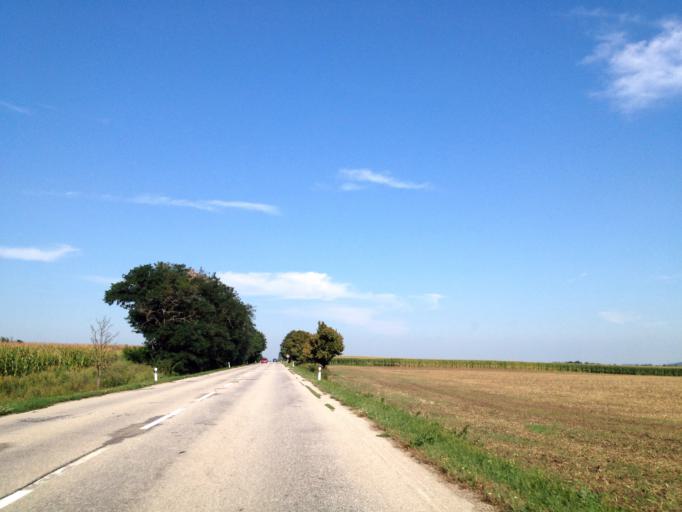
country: SK
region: Nitriansky
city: Svodin
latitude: 47.8998
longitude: 18.3628
